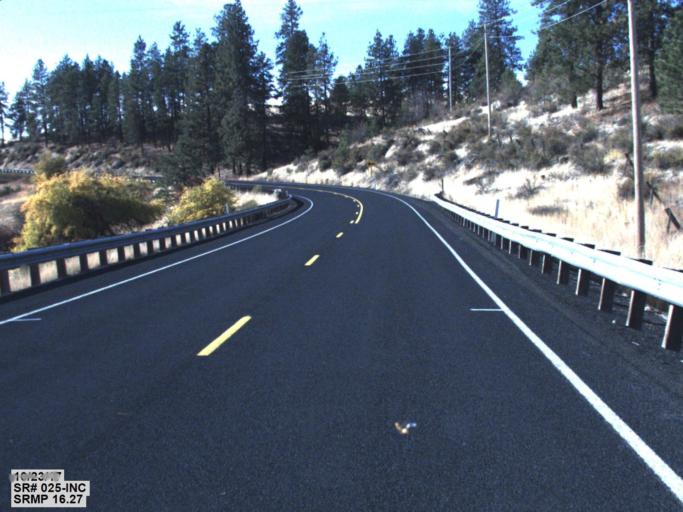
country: US
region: Washington
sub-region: Lincoln County
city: Davenport
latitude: 47.8619
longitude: -118.2301
